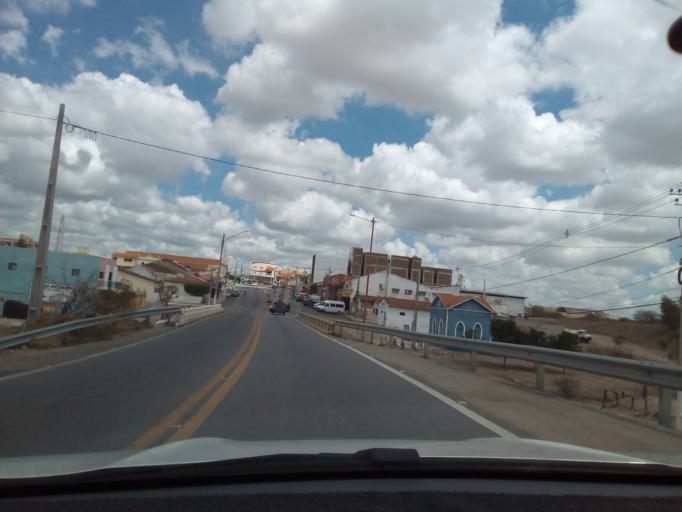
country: BR
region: Paraiba
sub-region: Soledade
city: Soledade
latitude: -7.0576
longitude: -36.3600
